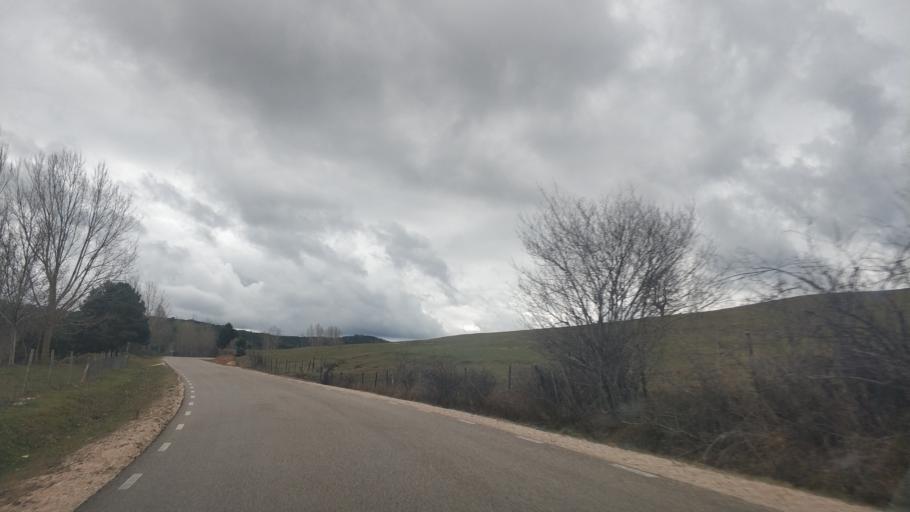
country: ES
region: Castille and Leon
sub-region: Provincia de Burgos
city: Canicosa de la Sierra
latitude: 41.9432
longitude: -3.0368
